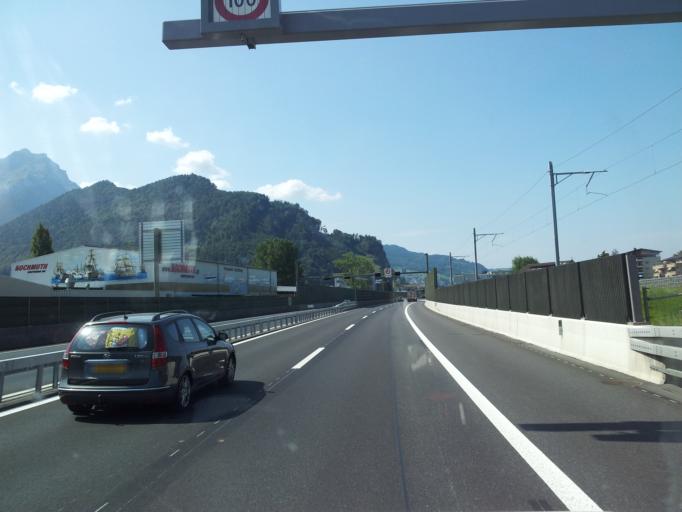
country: CH
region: Nidwalden
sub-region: Nidwalden
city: Stansstad
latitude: 46.9704
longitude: 8.3441
